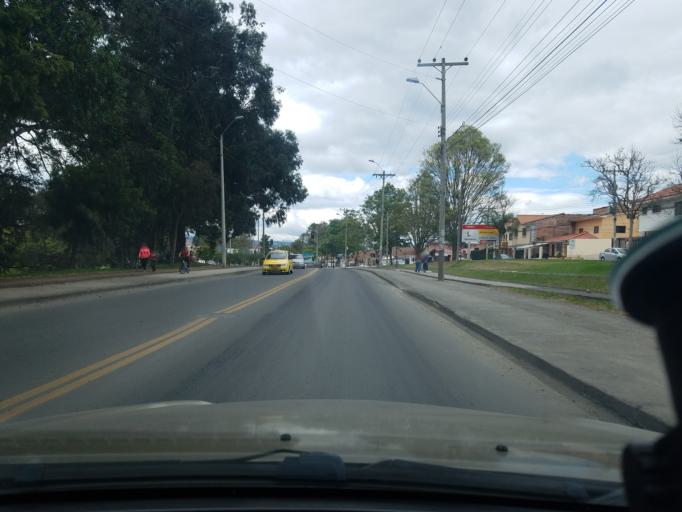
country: EC
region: Azuay
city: Cuenca
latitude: -2.9050
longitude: -78.9805
